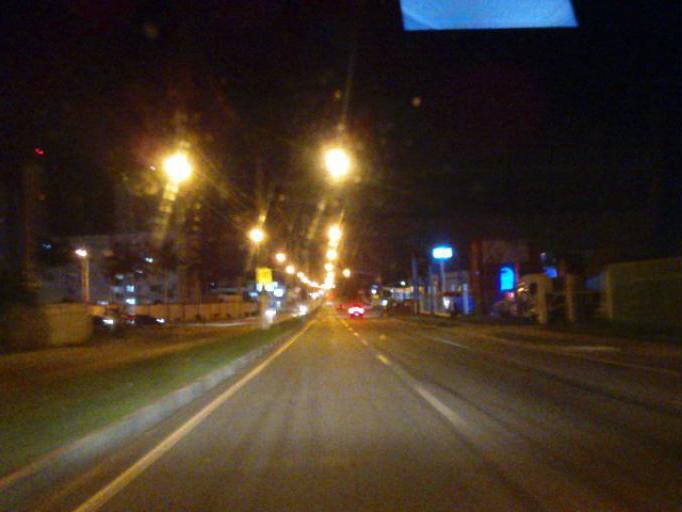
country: BR
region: Sao Paulo
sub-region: Jacarei
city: Jacarei
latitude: -23.2679
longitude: -45.9504
